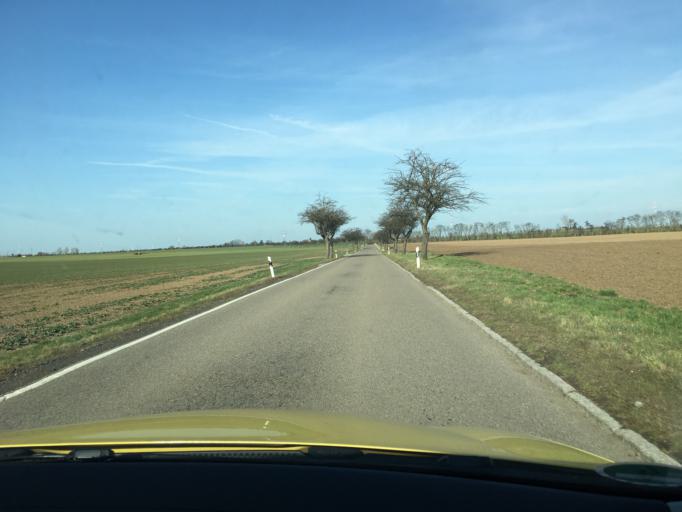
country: DE
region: Saxony-Anhalt
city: Laucha
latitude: 51.2427
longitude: 11.7030
